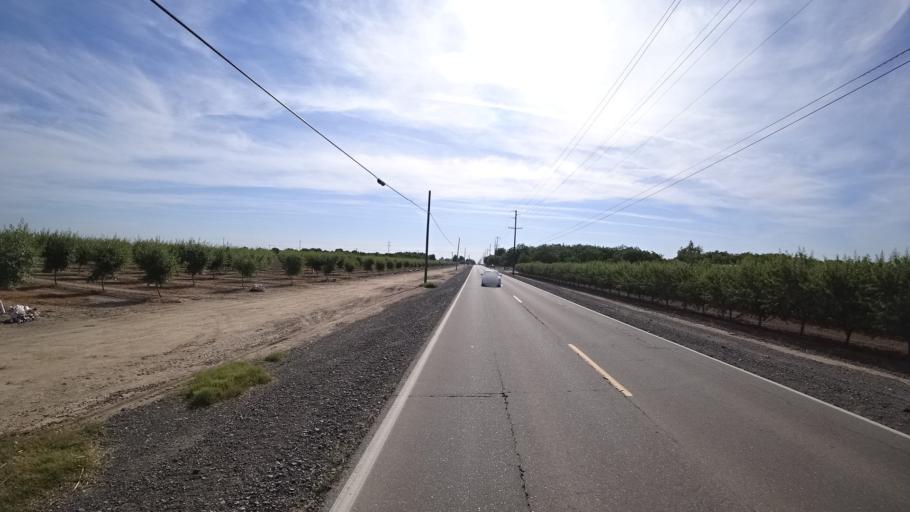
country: US
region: California
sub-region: Kings County
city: Hanford
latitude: 36.3427
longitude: -119.5867
